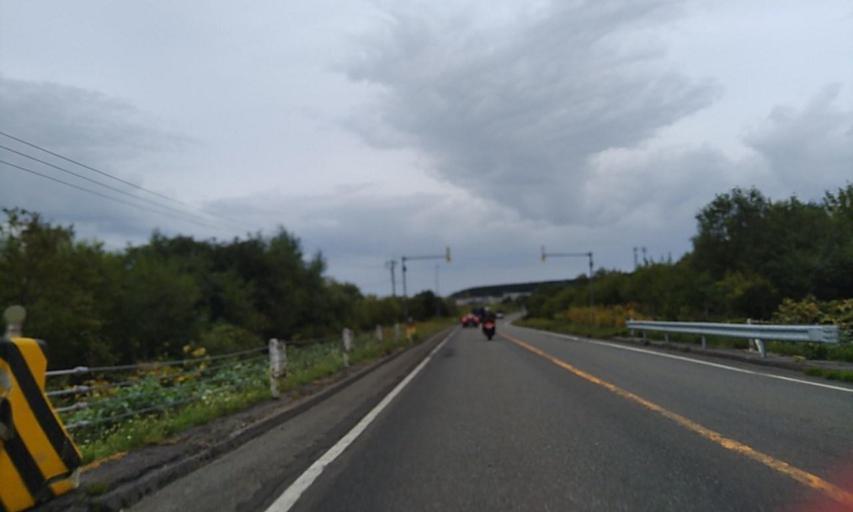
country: JP
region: Hokkaido
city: Nayoro
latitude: 44.9651
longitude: 142.5702
